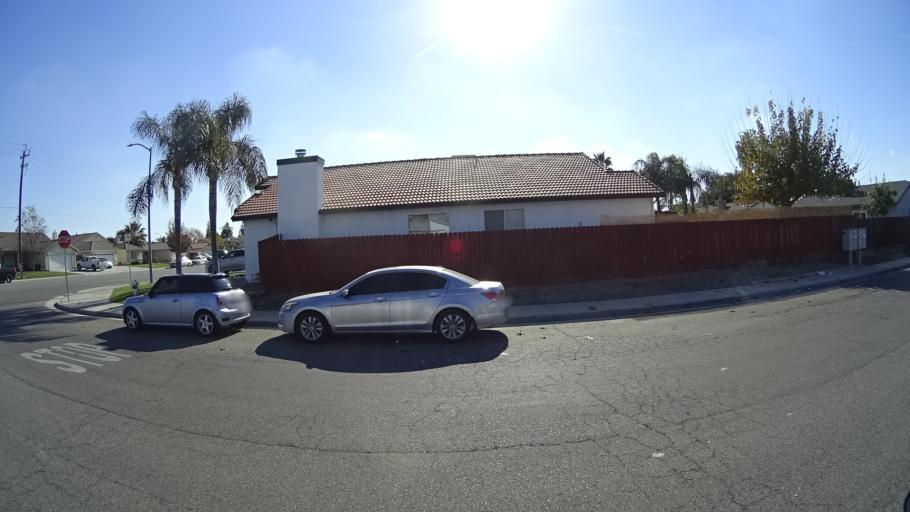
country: US
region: California
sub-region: Kern County
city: Greenfield
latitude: 35.2902
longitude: -119.0482
